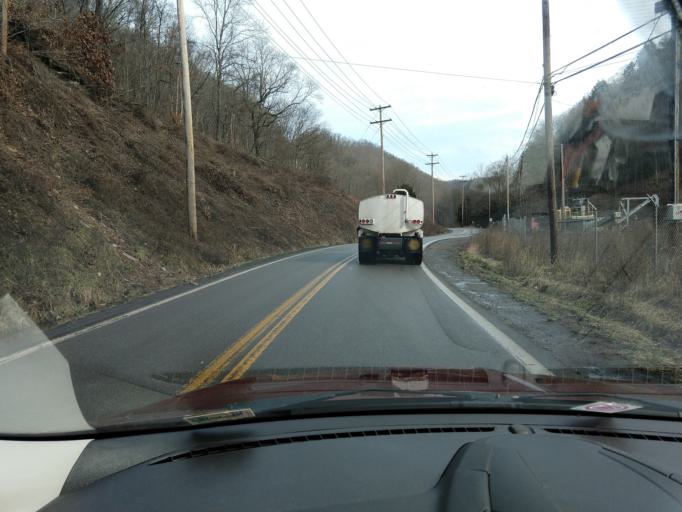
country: US
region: West Virginia
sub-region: McDowell County
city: Welch
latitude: 37.3339
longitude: -81.6803
